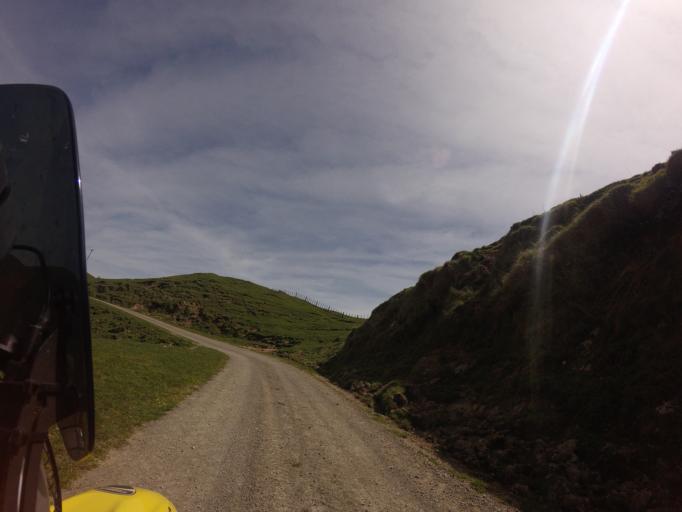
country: NZ
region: Bay of Plenty
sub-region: Opotiki District
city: Opotiki
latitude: -38.4524
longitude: 177.3618
